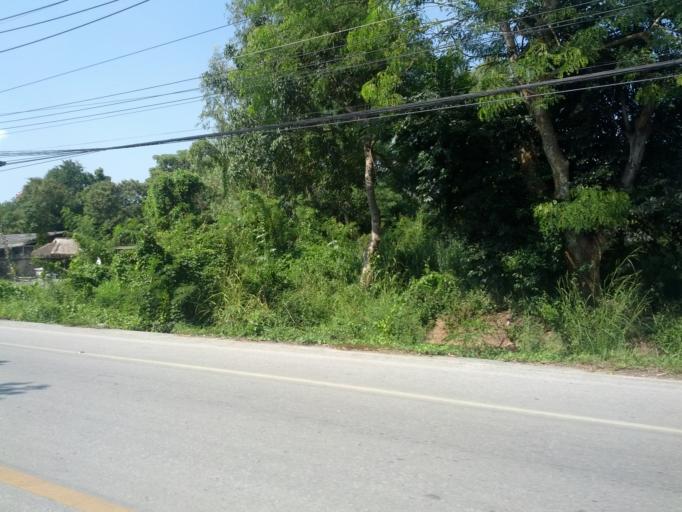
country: TH
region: Chiang Mai
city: San Kamphaeng
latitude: 18.7966
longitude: 99.1075
